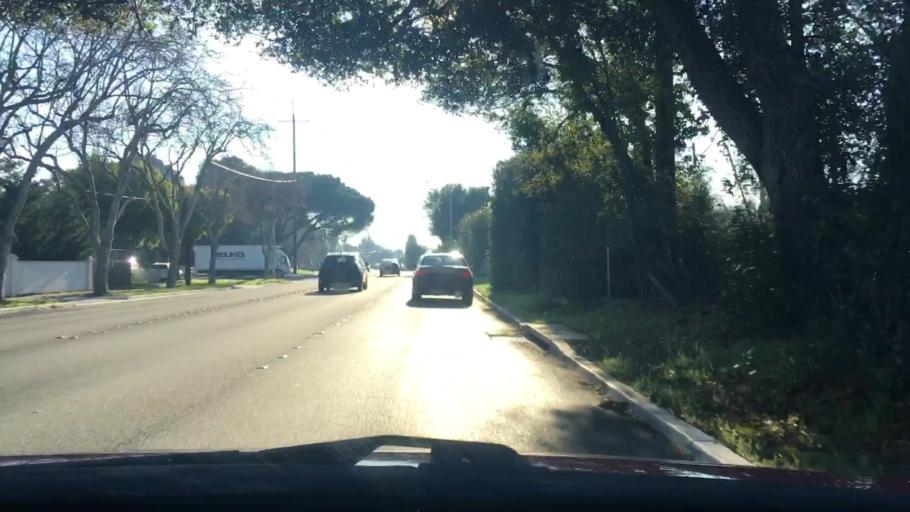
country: US
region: California
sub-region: Santa Clara County
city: Palo Alto
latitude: 37.4301
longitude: -122.1429
